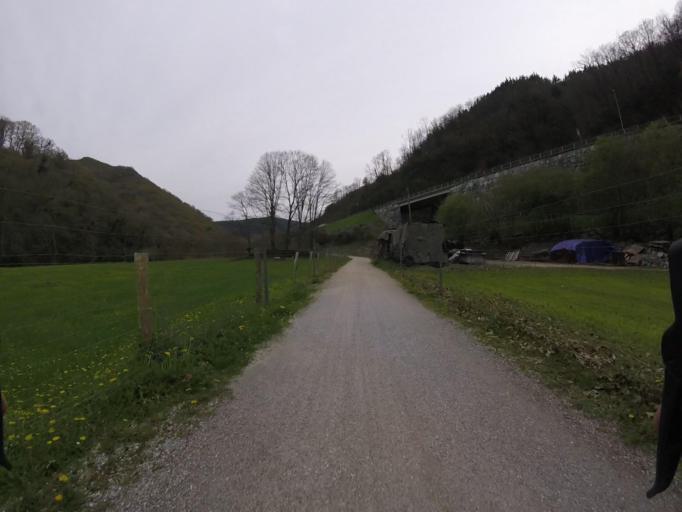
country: ES
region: Navarre
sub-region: Provincia de Navarra
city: Bera
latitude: 43.3073
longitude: -1.7355
